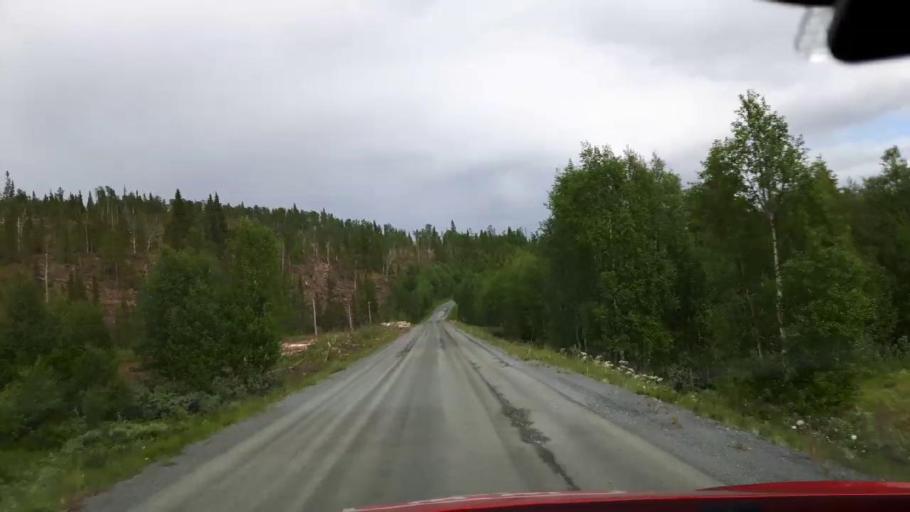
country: NO
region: Nord-Trondelag
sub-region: Lierne
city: Sandvika
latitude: 64.1488
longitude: 13.9617
